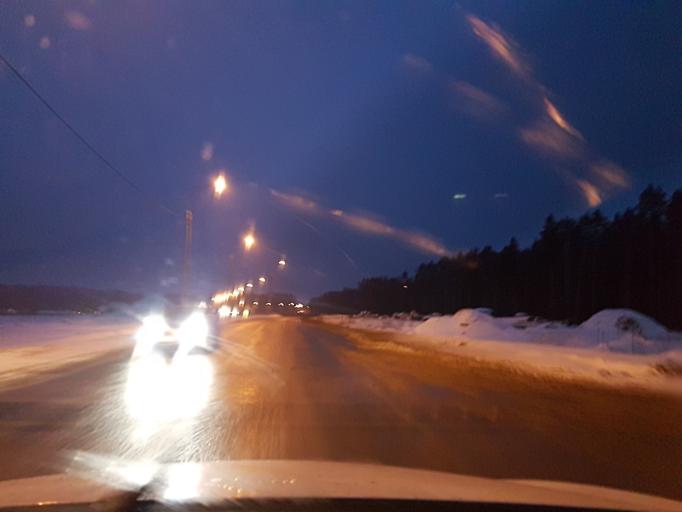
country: RU
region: Tverskaya
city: Novozavidovskiy
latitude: 56.5757
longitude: 36.4751
